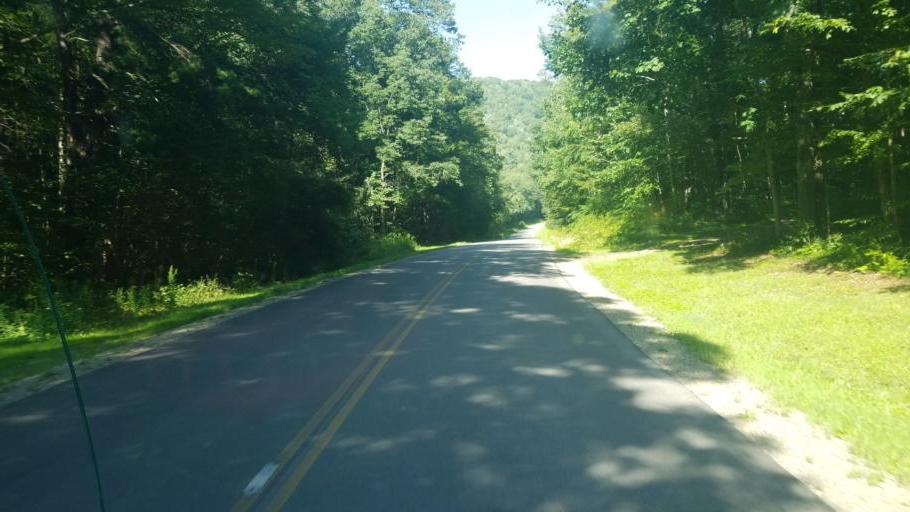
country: US
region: New York
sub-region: Allegany County
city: Wellsville
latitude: 42.0198
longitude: -77.9857
